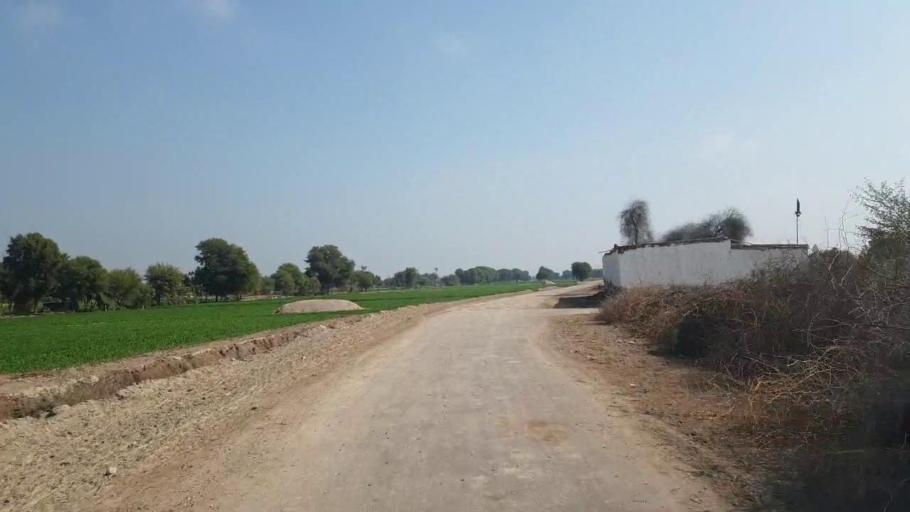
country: PK
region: Sindh
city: Shahdadpur
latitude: 26.0304
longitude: 68.6163
